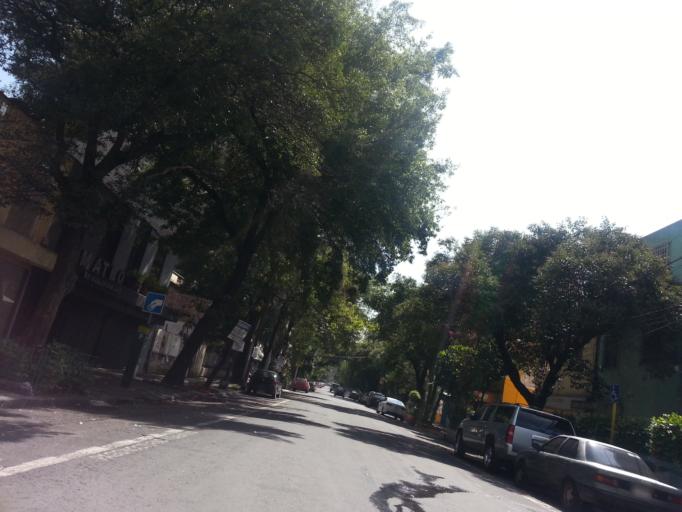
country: MX
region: Mexico City
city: Benito Juarez
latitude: 19.4200
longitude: -99.1711
